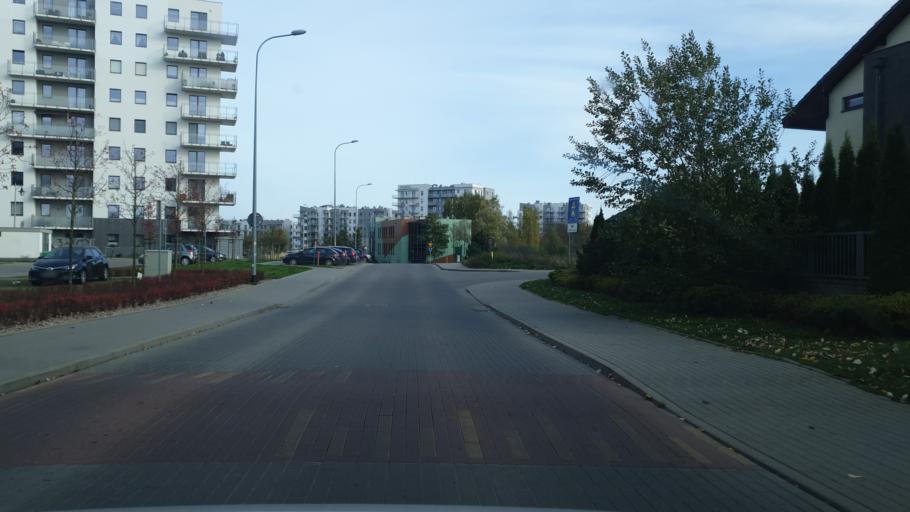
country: PL
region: Pomeranian Voivodeship
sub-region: Powiat gdanski
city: Kowale
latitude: 54.3488
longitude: 18.5887
